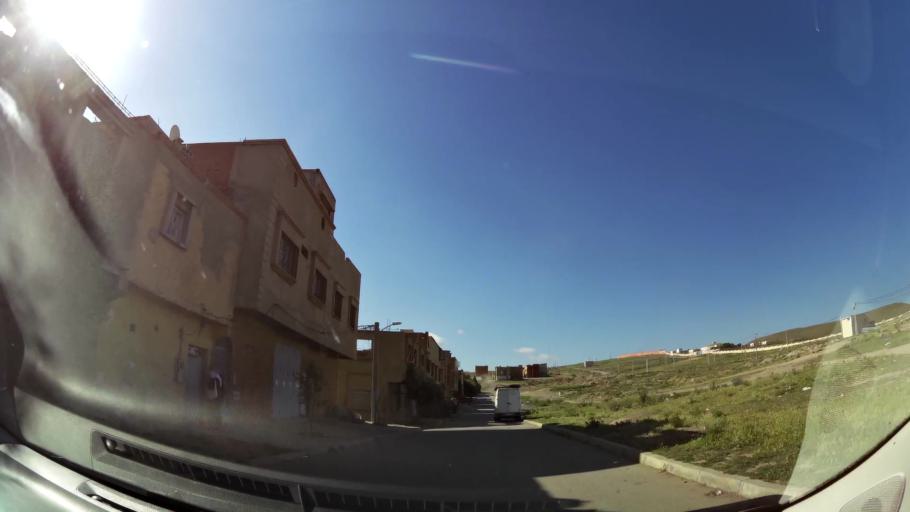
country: MA
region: Oriental
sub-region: Oujda-Angad
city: Oujda
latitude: 34.6552
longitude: -1.9515
